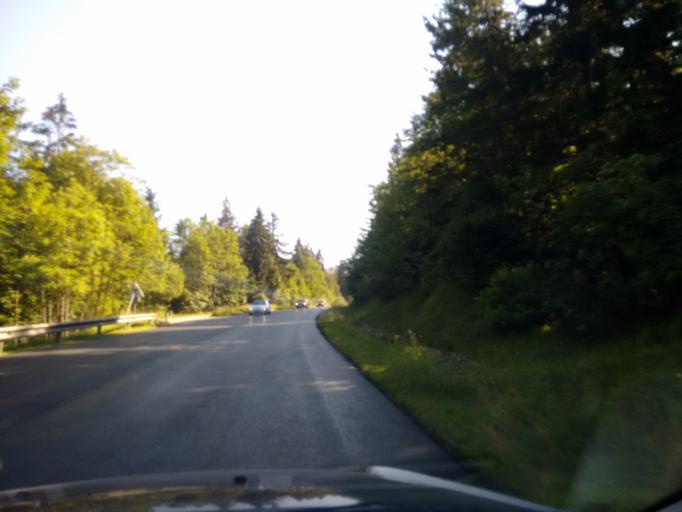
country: AT
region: Upper Austria
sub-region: Politischer Bezirk Gmunden
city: Bad Goisern
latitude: 47.6161
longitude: 13.6658
